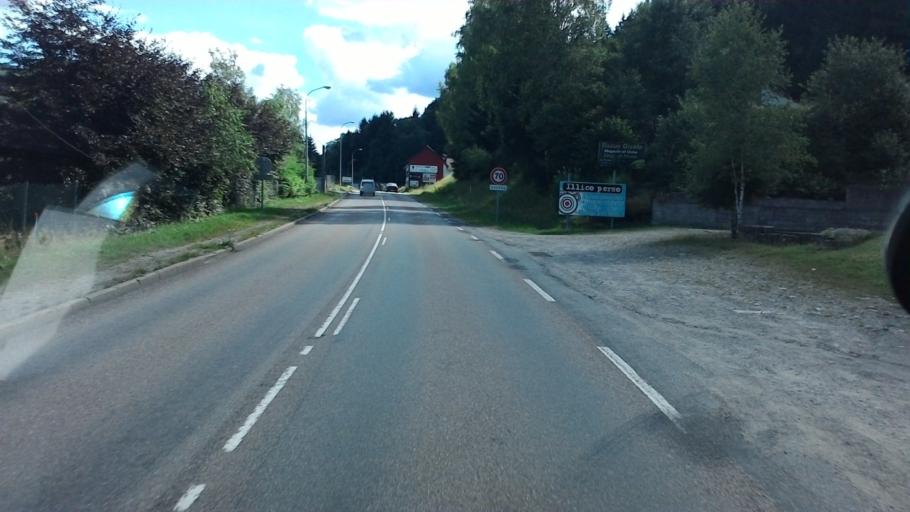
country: FR
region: Lorraine
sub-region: Departement des Vosges
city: La Bresse
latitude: 47.9932
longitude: 6.8537
